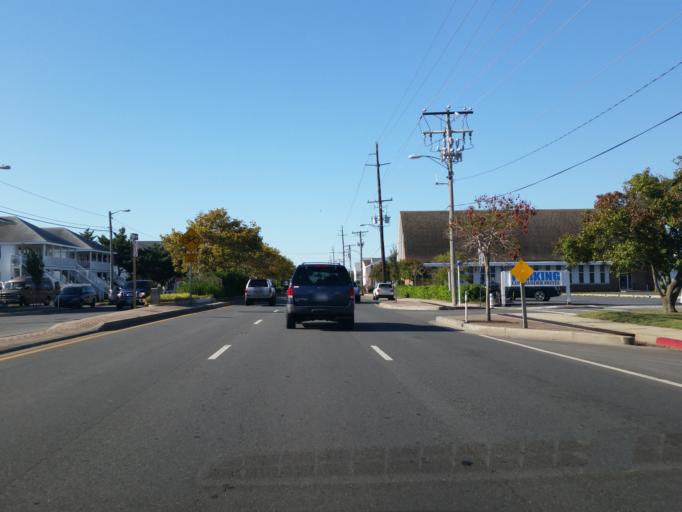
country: US
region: Maryland
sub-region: Worcester County
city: Ocean City
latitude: 38.3449
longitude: -75.0805
